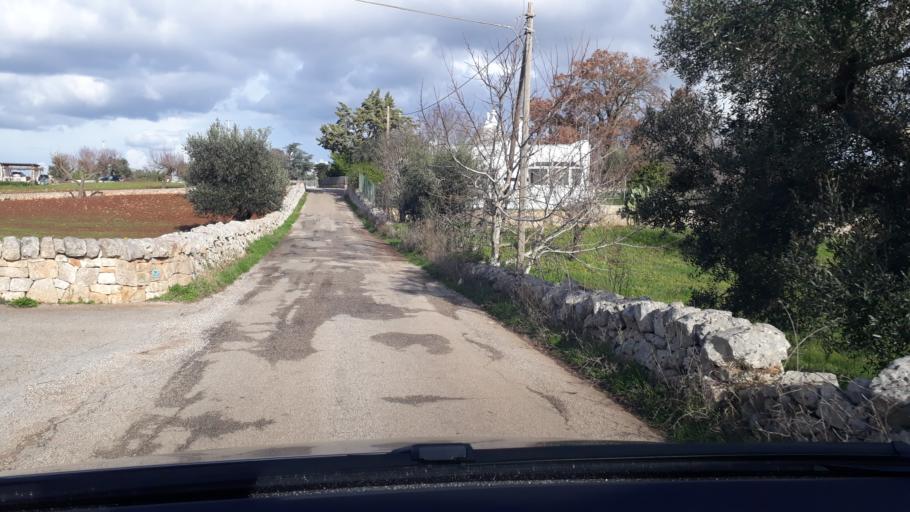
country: IT
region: Apulia
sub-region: Provincia di Brindisi
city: Cisternino
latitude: 40.7110
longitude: 17.4222
